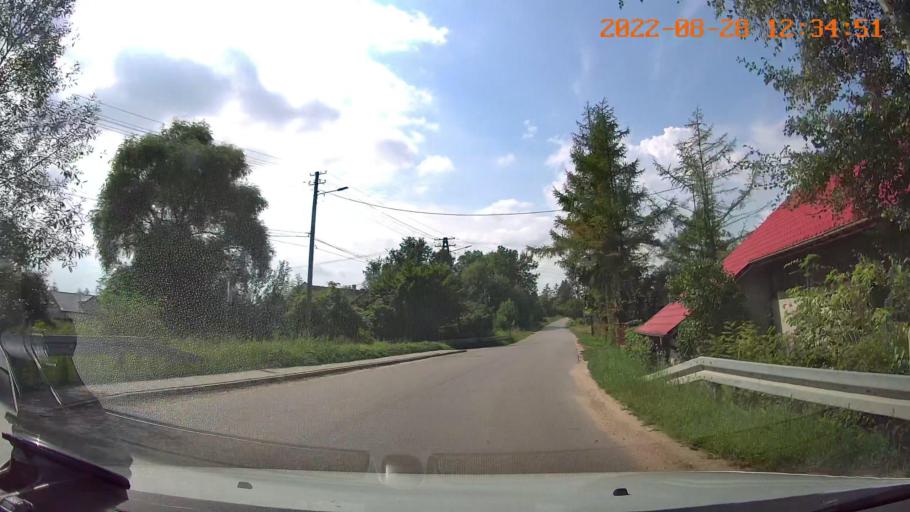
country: PL
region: Swietokrzyskie
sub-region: Powiat kazimierski
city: Skalbmierz
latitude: 50.3764
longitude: 20.4277
